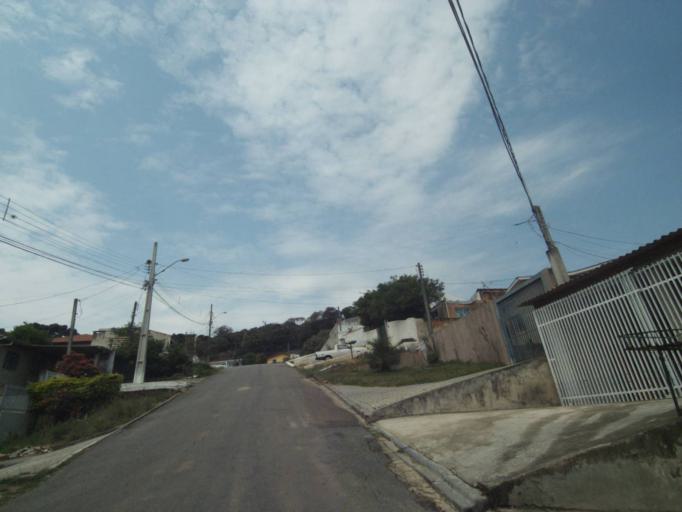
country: BR
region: Parana
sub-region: Curitiba
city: Curitiba
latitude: -25.4736
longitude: -49.3222
